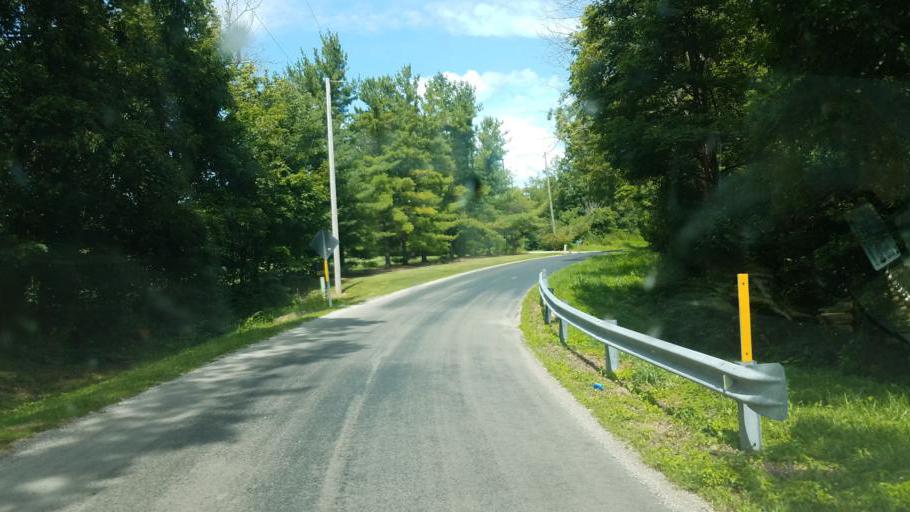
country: US
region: Ohio
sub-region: Delaware County
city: Sunbury
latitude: 40.2580
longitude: -82.8435
